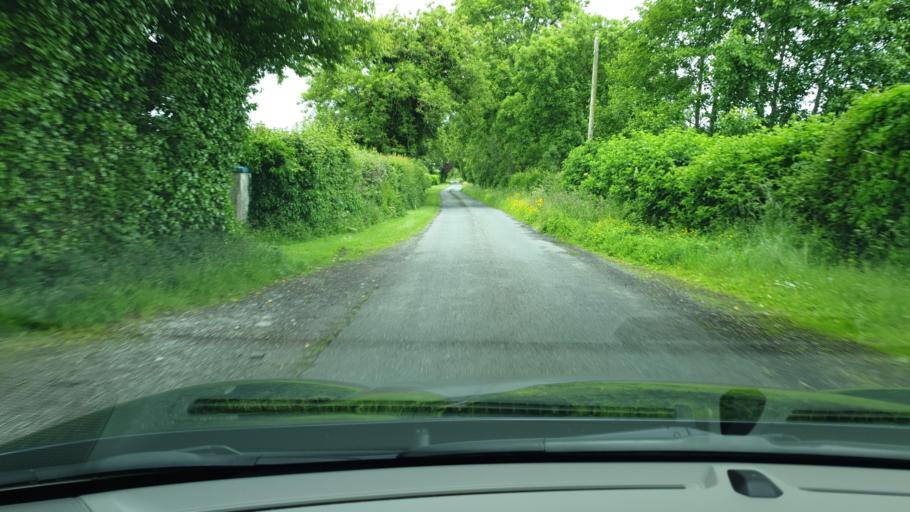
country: IE
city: Confey
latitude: 53.4094
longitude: -6.5252
